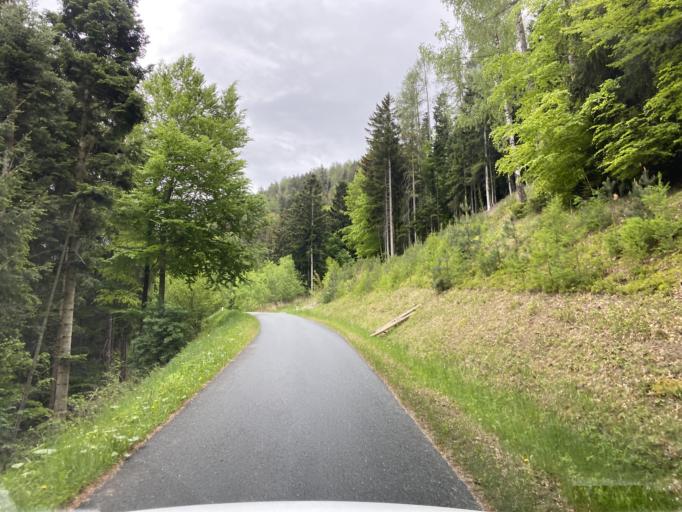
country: AT
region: Styria
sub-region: Politischer Bezirk Weiz
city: Koglhof
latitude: 47.3314
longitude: 15.6634
